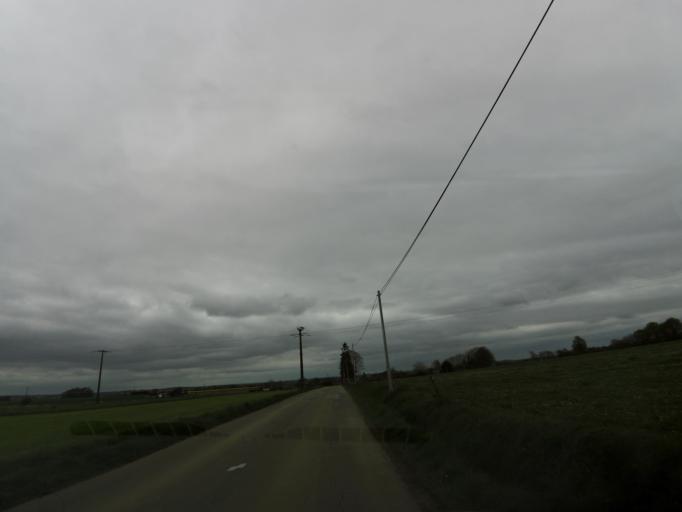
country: FR
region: Brittany
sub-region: Departement d'Ille-et-Vilaine
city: Janze
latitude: 47.9954
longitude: -1.5212
